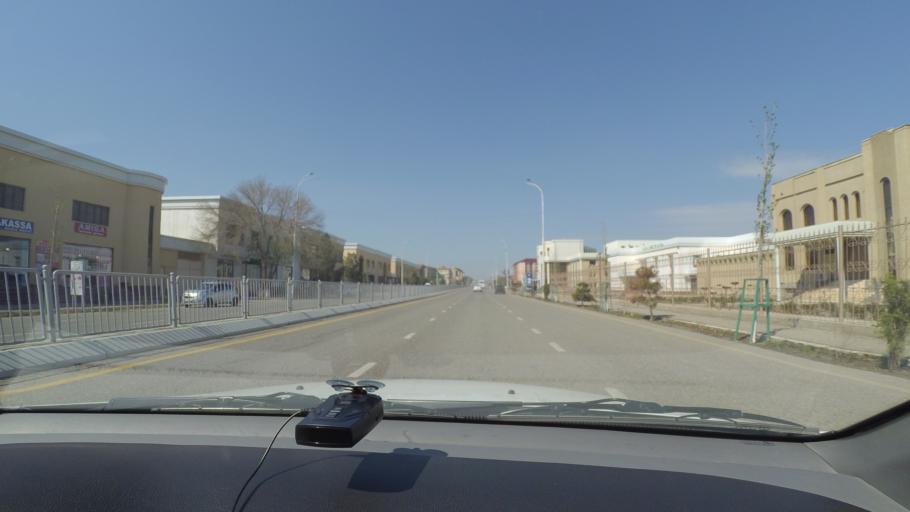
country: UZ
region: Bukhara
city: Bukhara
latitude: 39.7676
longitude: 64.4598
